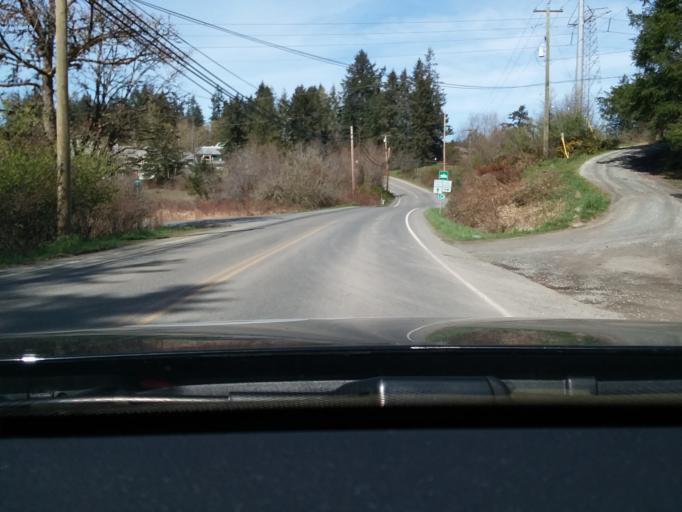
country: CA
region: British Columbia
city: North Cowichan
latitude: 48.8645
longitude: -123.5013
